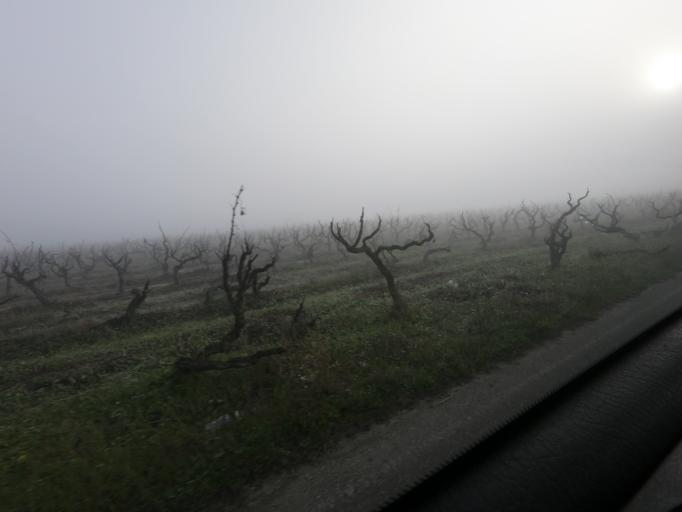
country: PT
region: Setubal
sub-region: Palmela
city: Palmela
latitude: 38.6012
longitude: -8.8472
